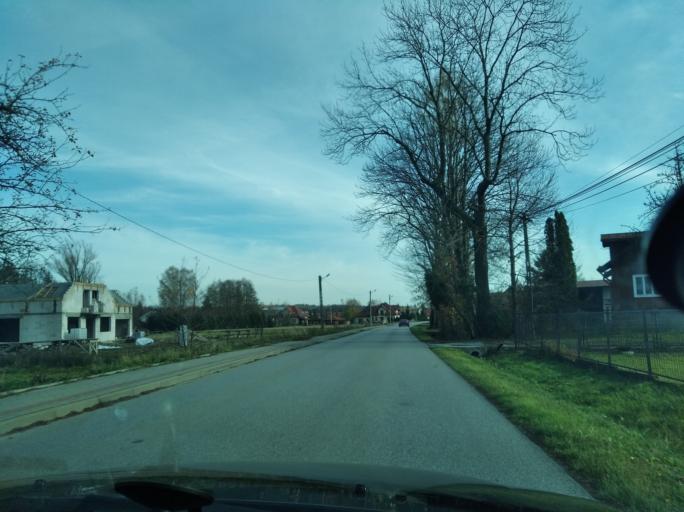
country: PL
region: Subcarpathian Voivodeship
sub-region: Powiat lancucki
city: Kraczkowa
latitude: 50.0375
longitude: 22.1490
